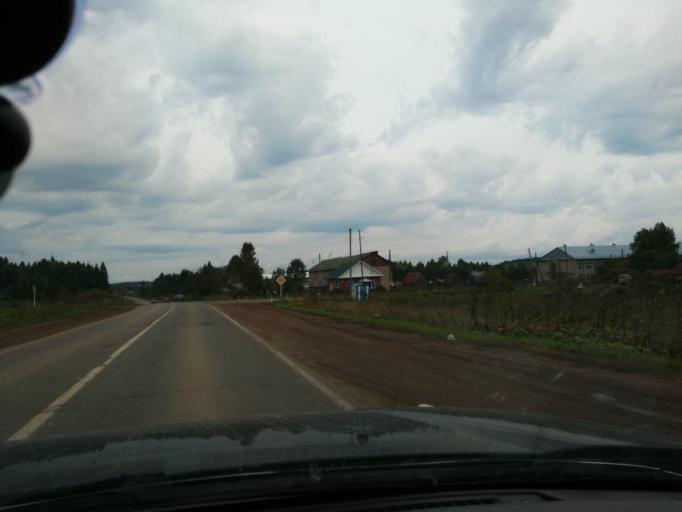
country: RU
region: Perm
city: Chernushka
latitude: 56.7317
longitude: 56.1758
